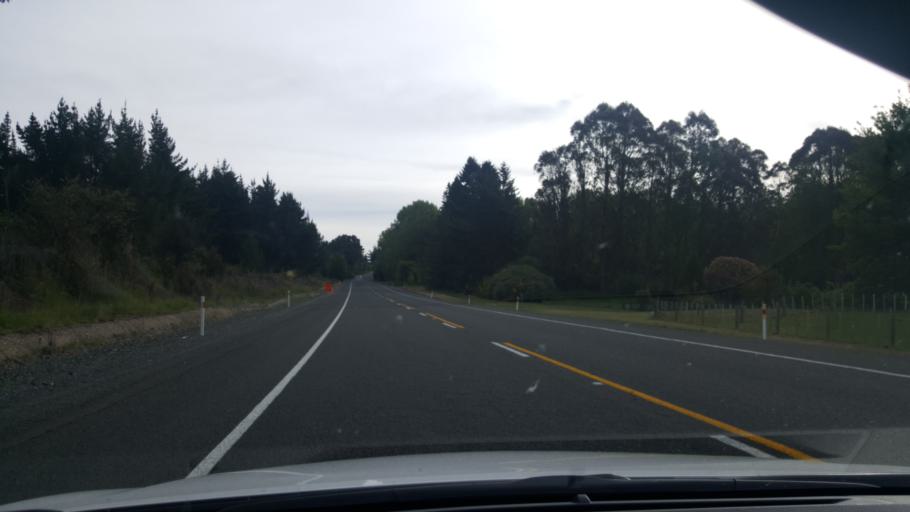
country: NZ
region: Waikato
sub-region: Taupo District
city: Taupo
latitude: -38.6162
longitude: 176.1121
